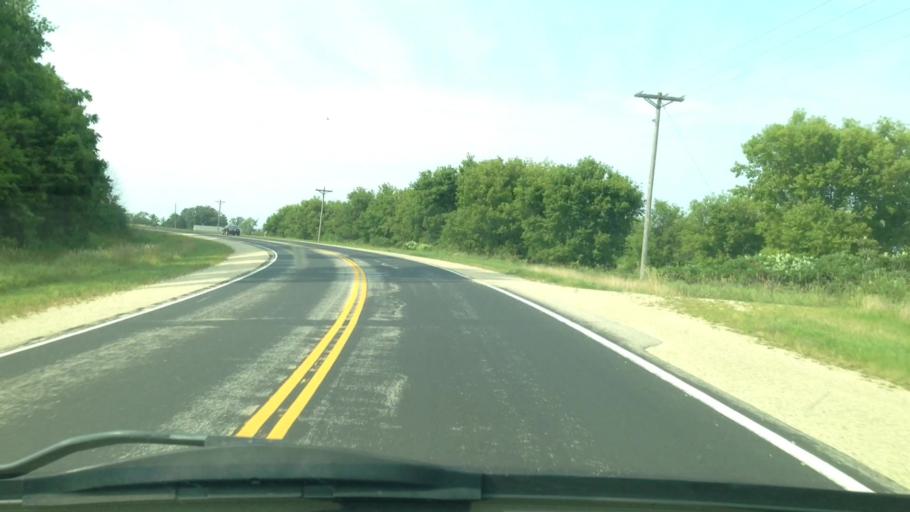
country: US
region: Minnesota
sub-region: Winona County
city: Lewiston
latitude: 43.9258
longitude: -91.9576
